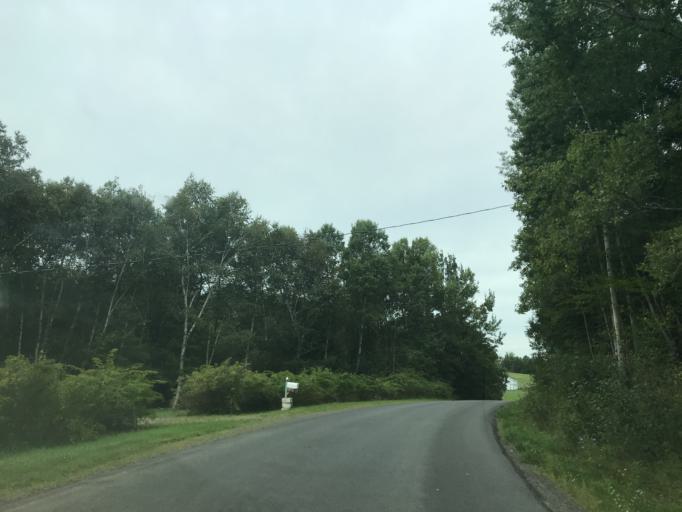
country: US
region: New York
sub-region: Otsego County
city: Worcester
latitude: 42.5905
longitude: -74.6805
